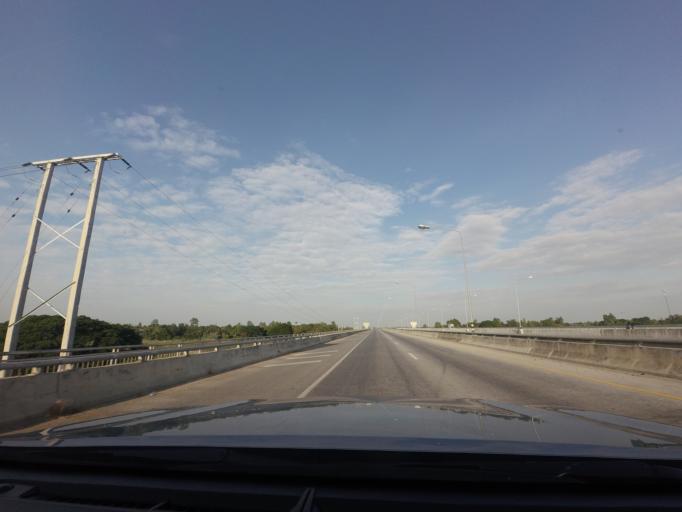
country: TH
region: Nakhon Sawan
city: Nakhon Sawan
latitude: 15.7524
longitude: 100.0851
